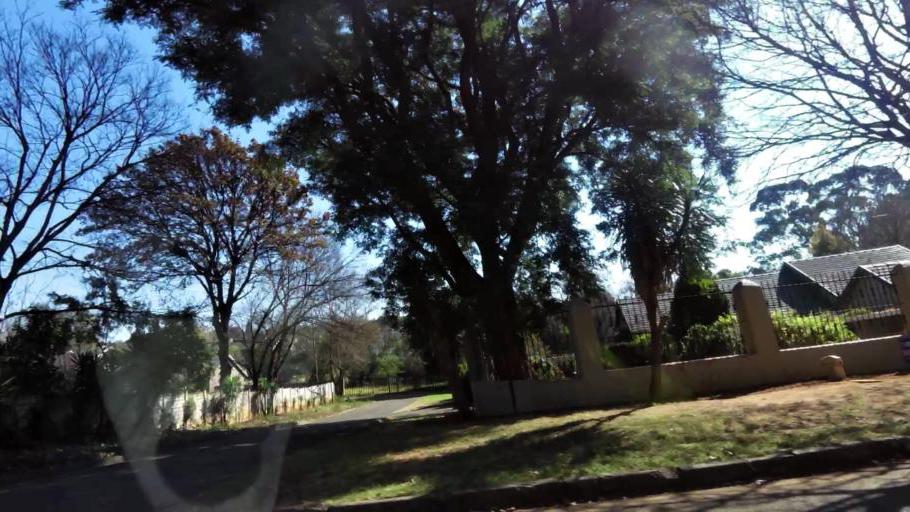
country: ZA
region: Gauteng
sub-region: City of Johannesburg Metropolitan Municipality
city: Roodepoort
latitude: -26.1345
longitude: 27.9509
